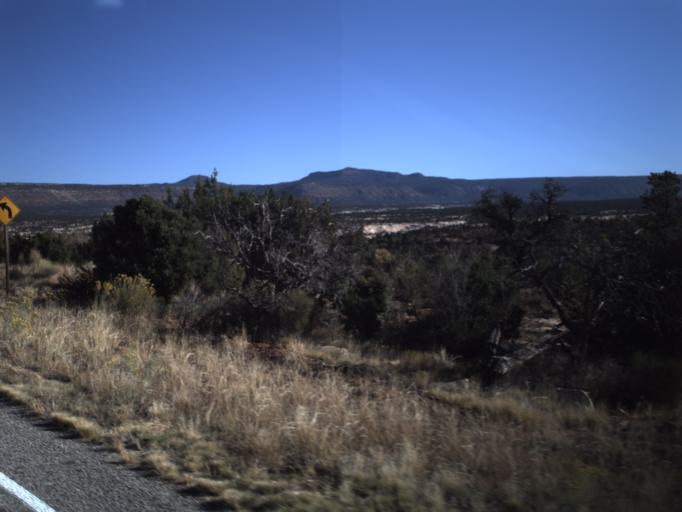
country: US
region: Utah
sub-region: San Juan County
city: Blanding
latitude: 37.5838
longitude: -110.0398
